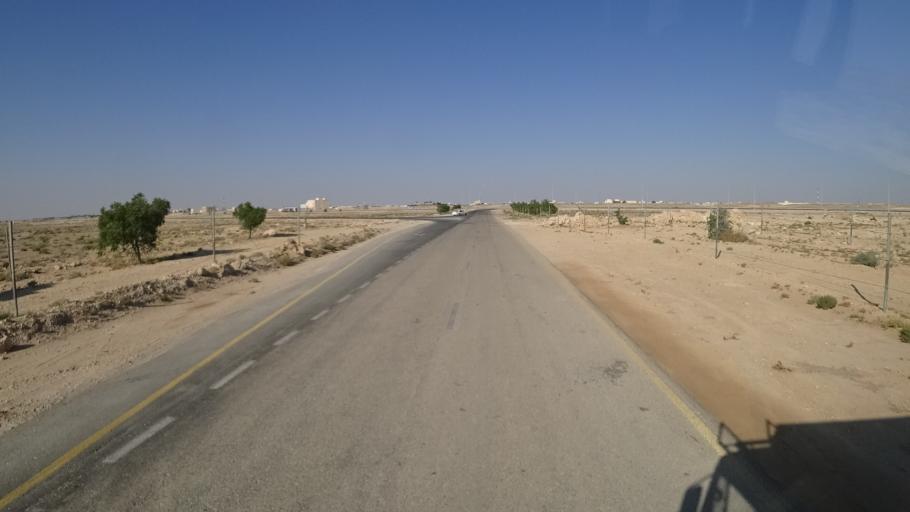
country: OM
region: Zufar
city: Salalah
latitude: 17.5977
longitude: 54.0349
